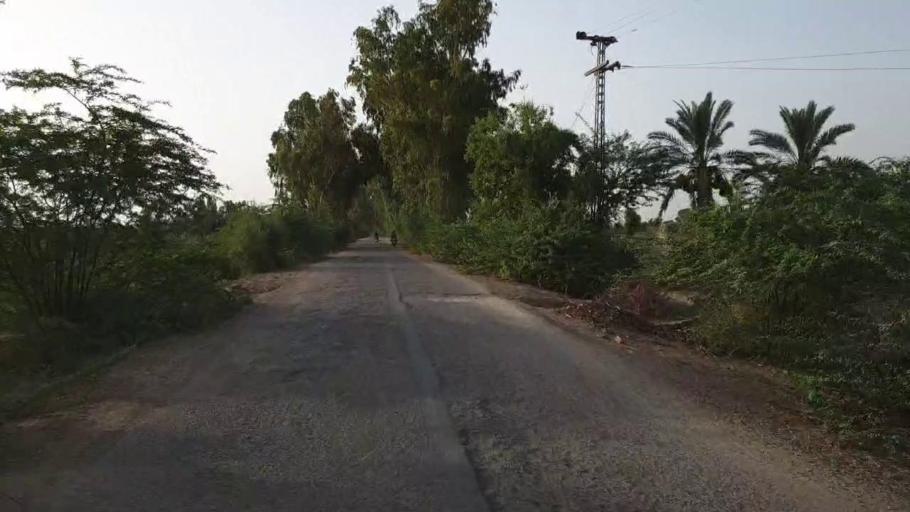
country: PK
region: Sindh
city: Bozdar
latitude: 27.1132
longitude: 68.9587
